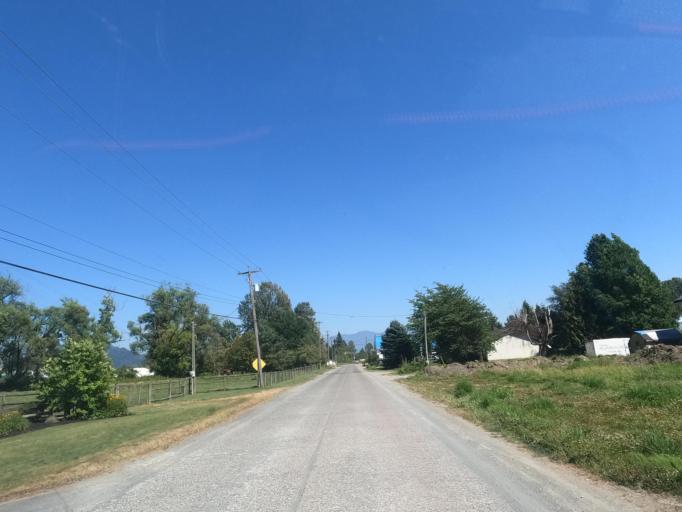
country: CA
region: British Columbia
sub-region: Fraser Valley Regional District
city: Chilliwack
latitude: 49.1256
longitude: -122.0925
